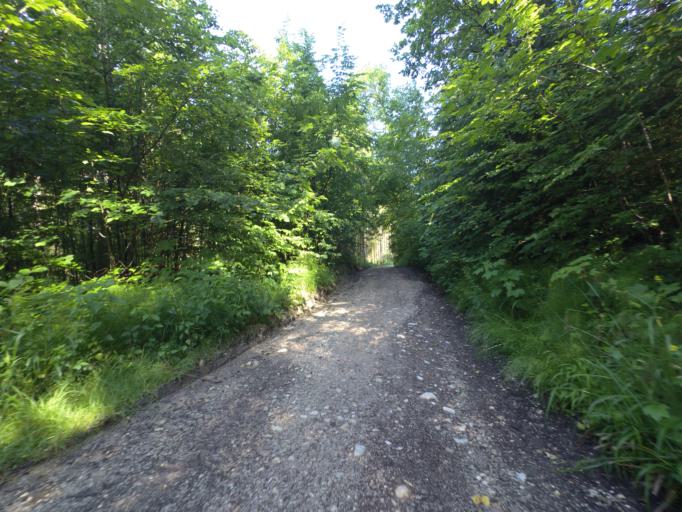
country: AT
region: Salzburg
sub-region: Politischer Bezirk Salzburg-Umgebung
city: Grodig
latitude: 47.7524
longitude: 12.9908
